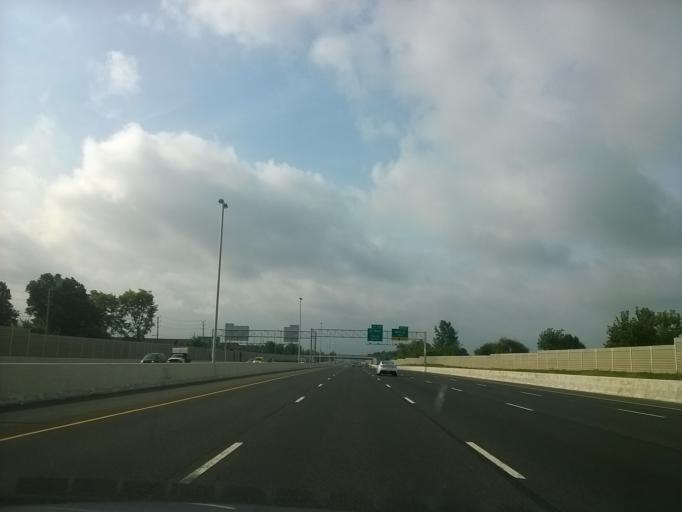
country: US
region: Indiana
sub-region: Marion County
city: Speedway
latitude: 39.8435
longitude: -86.2762
